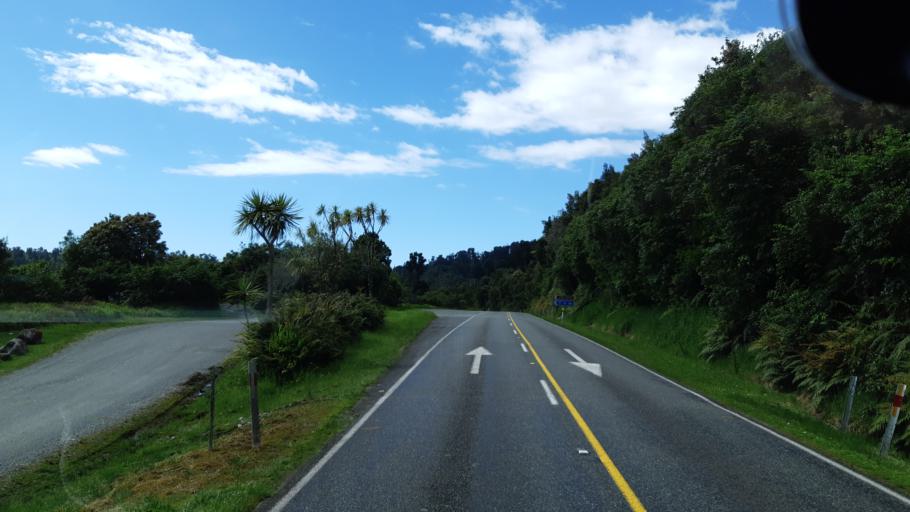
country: NZ
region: West Coast
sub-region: Westland District
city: Hokitika
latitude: -43.0590
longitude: 170.6349
